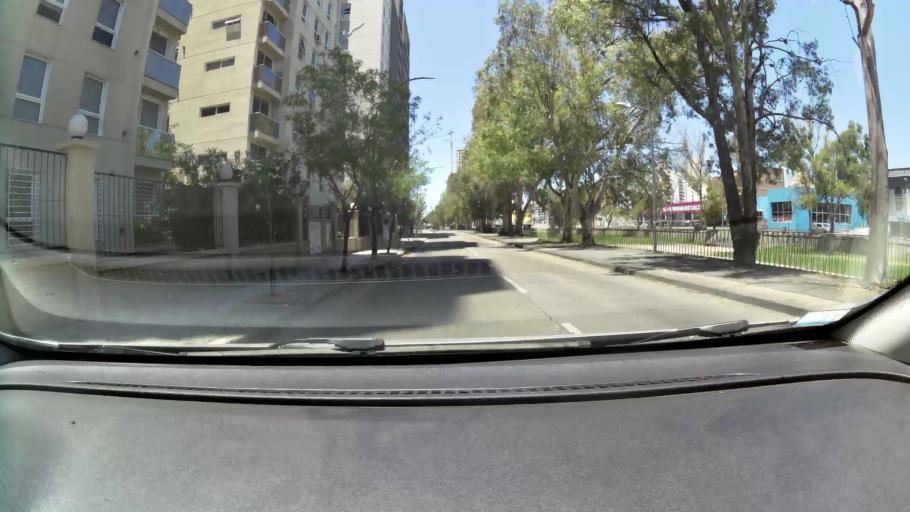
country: AR
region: Cordoba
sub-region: Departamento de Capital
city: Cordoba
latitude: -31.4051
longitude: -64.1971
